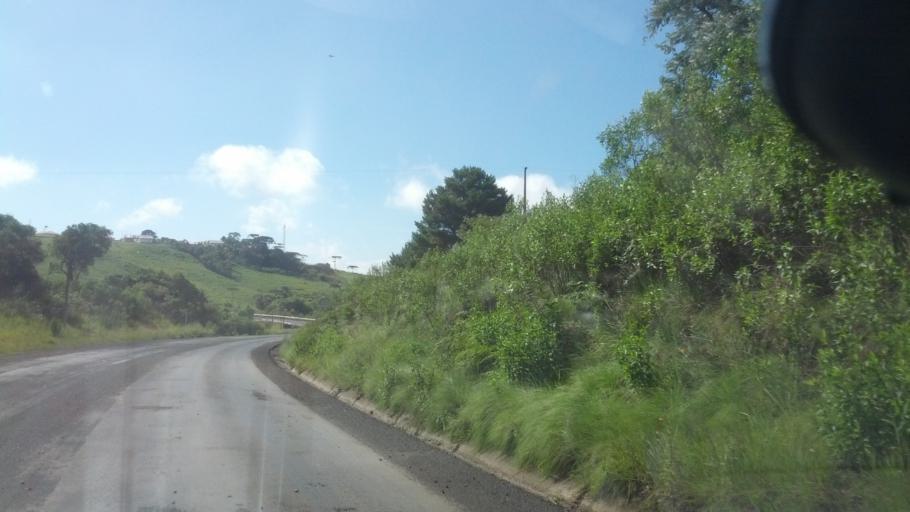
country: BR
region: Santa Catarina
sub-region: Lages
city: Lages
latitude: -27.9359
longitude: -50.5206
